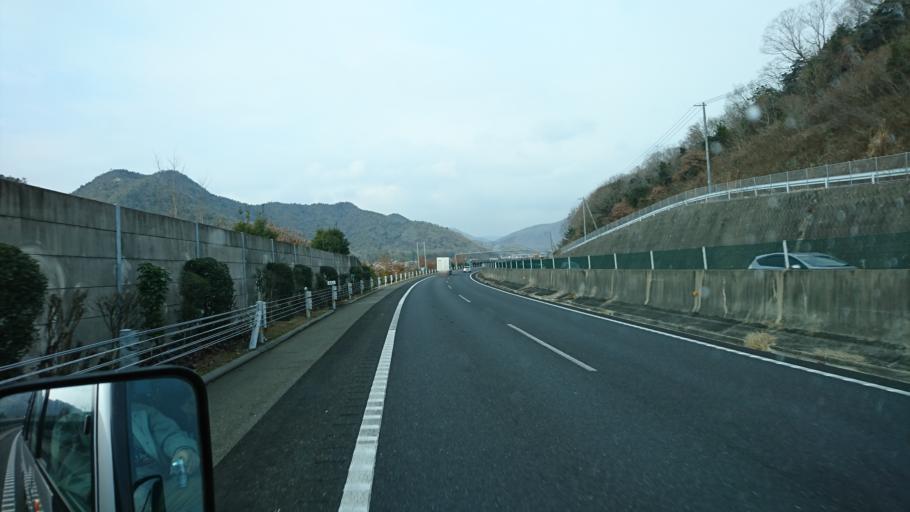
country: JP
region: Hyogo
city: Kakogawacho-honmachi
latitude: 34.8486
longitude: 134.7967
